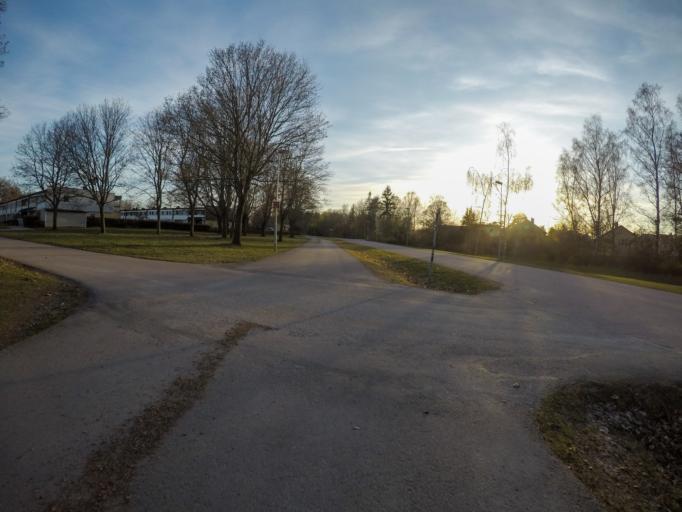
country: SE
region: Vaestmanland
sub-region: Vasteras
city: Vasteras
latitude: 59.5997
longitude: 16.6046
